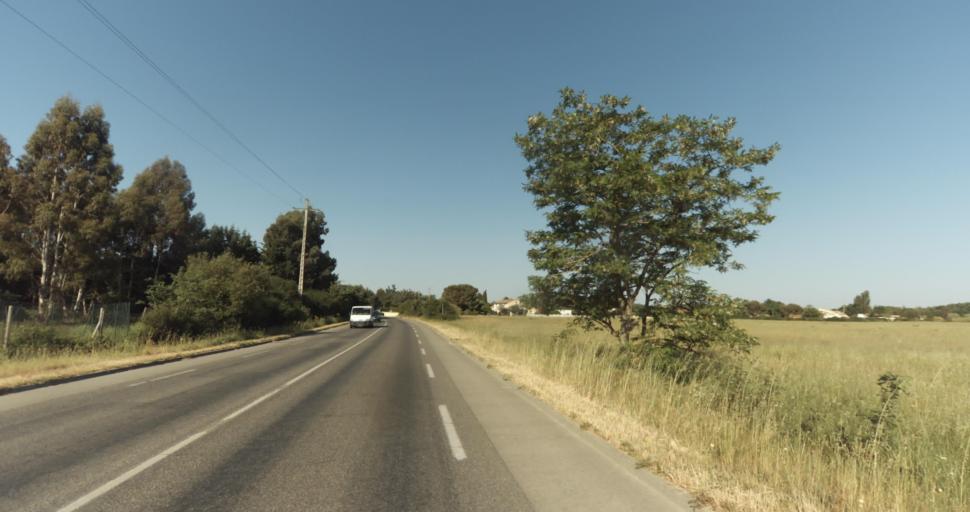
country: FR
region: Midi-Pyrenees
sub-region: Departement de la Haute-Garonne
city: Fonsorbes
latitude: 43.5541
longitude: 1.2519
